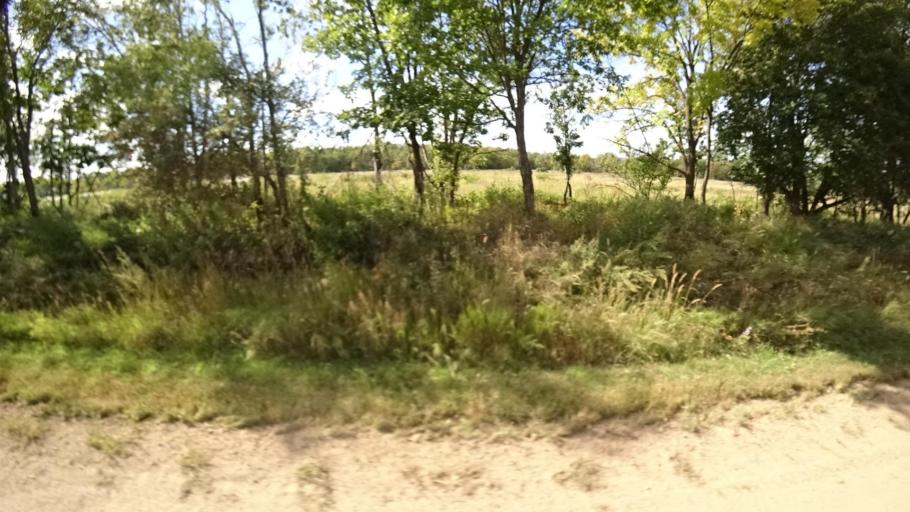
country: RU
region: Primorskiy
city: Yakovlevka
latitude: 44.4213
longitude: 133.5716
